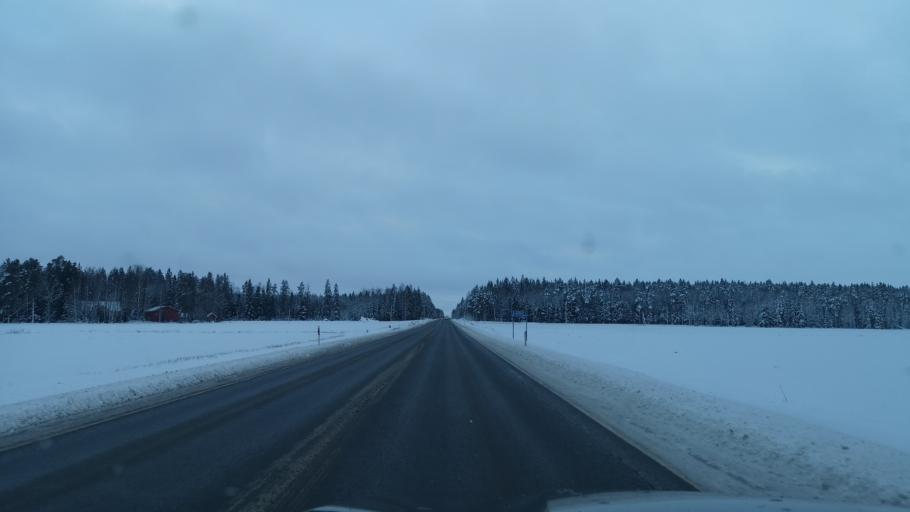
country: FI
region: Varsinais-Suomi
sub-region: Loimaa
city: Loimaa
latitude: 60.9065
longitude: 23.1560
